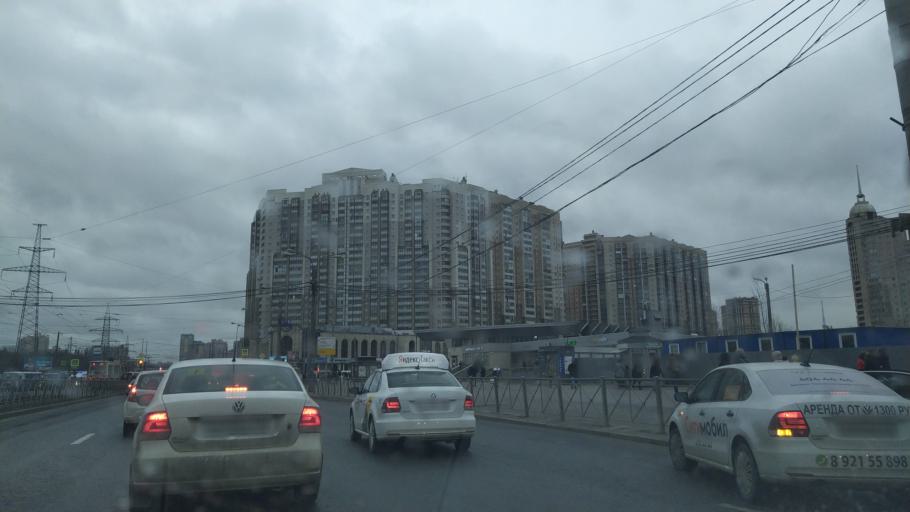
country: RU
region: St.-Petersburg
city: Novaya Derevnya
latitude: 60.0033
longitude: 30.2952
